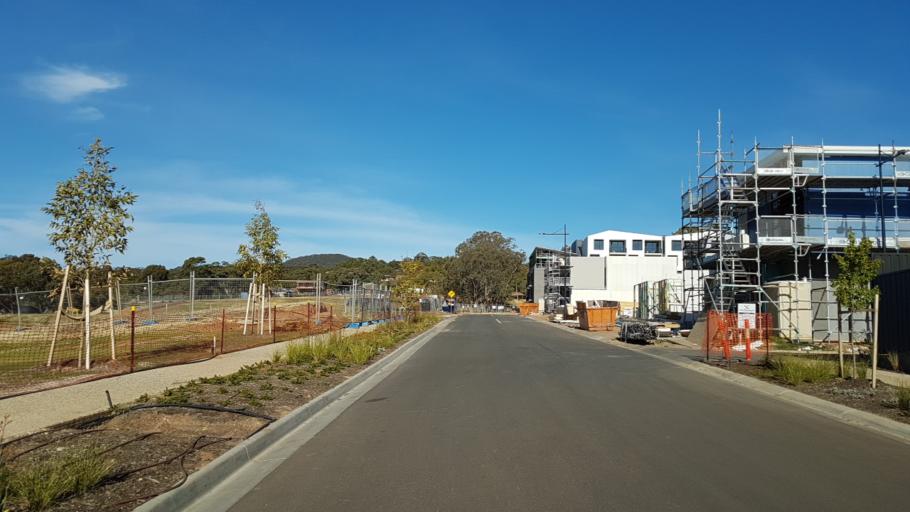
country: AU
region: South Australia
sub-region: Burnside
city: Wattle Park
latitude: -34.9055
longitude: 138.6855
